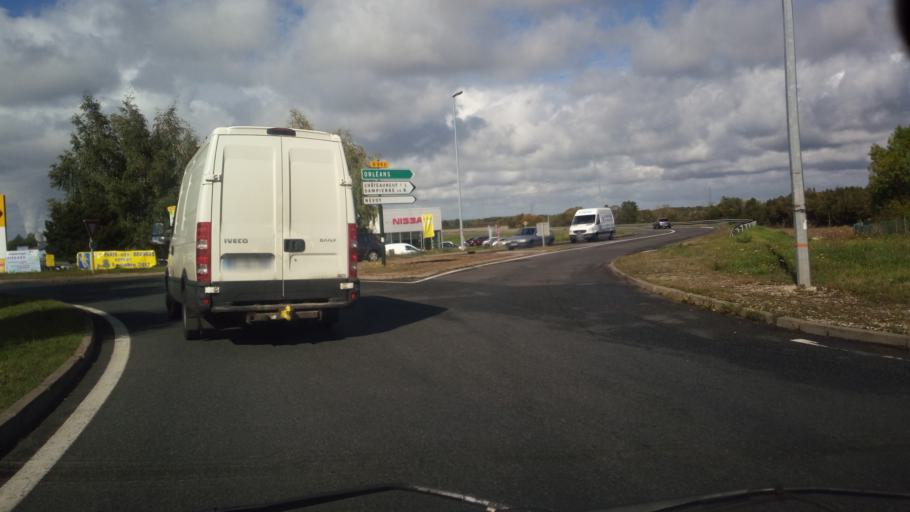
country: FR
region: Centre
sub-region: Departement du Loiret
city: Gien
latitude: 47.7089
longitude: 2.6416
